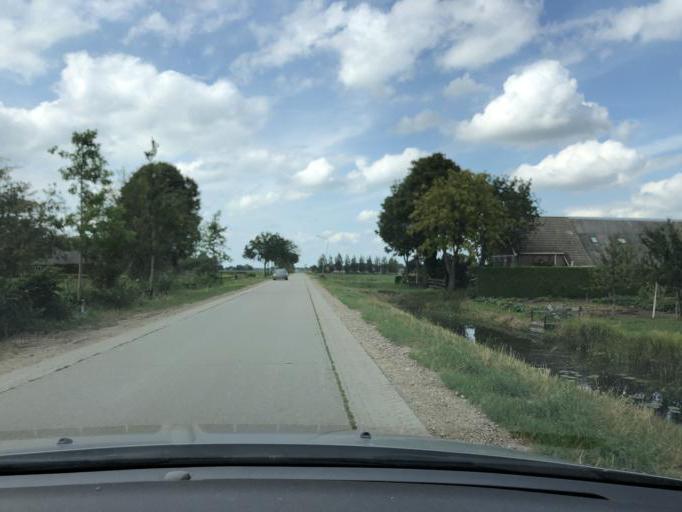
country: NL
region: Overijssel
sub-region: Gemeente Dalfsen
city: Dalfsen
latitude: 52.5637
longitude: 6.2018
